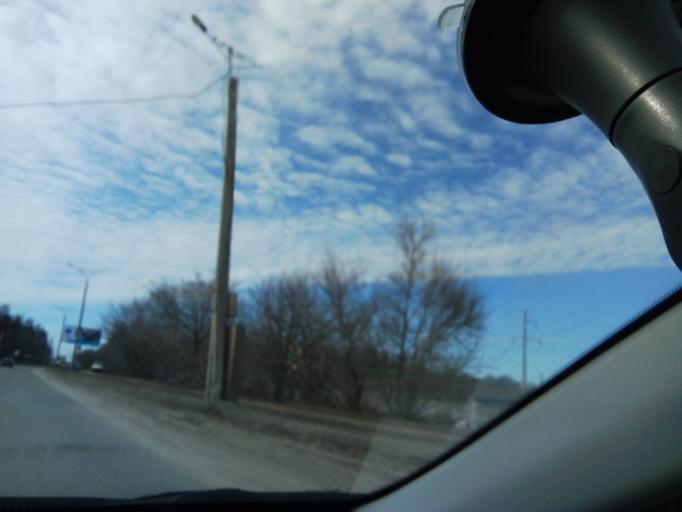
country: RU
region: Chuvashia
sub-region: Cheboksarskiy Rayon
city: Cheboksary
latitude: 56.0960
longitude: 47.2615
